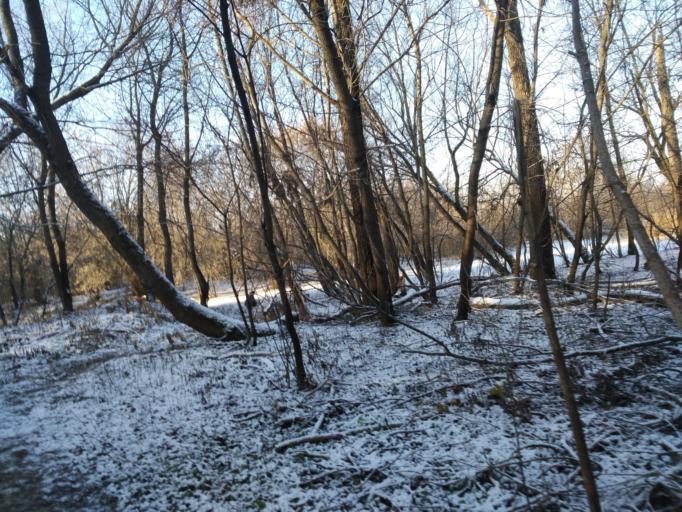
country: RU
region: Kirov
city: Vyatskiye Polyany
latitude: 56.2368
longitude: 51.0593
